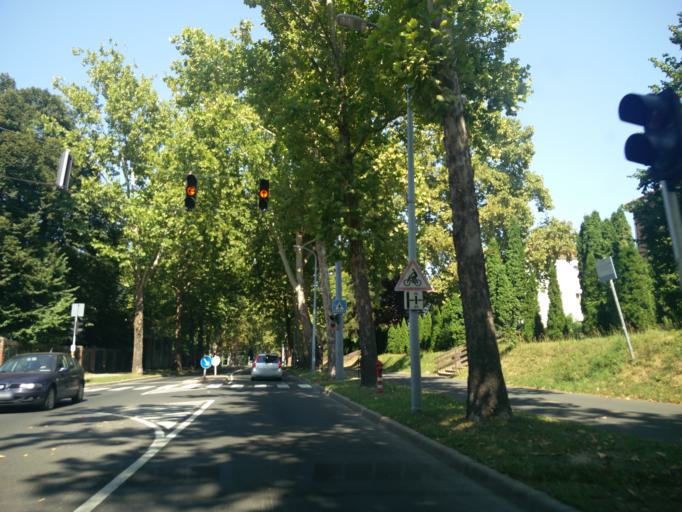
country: HU
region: Zala
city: Zalaegerszeg
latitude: 46.8403
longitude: 16.8343
